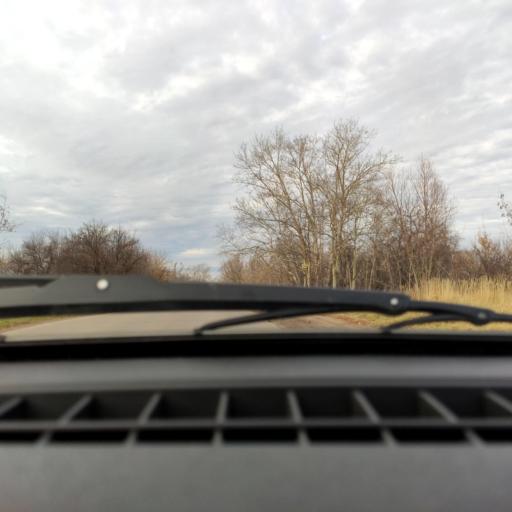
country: RU
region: Bashkortostan
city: Ufa
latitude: 54.8728
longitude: 56.1315
